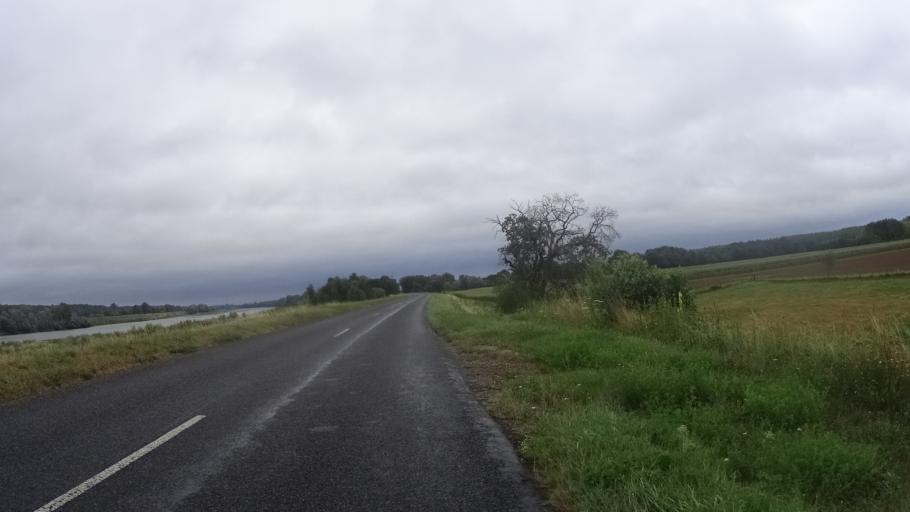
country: FR
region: Centre
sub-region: Departement du Loir-et-Cher
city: Chouzy-sur-Cisse
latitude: 47.5296
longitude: 1.2720
